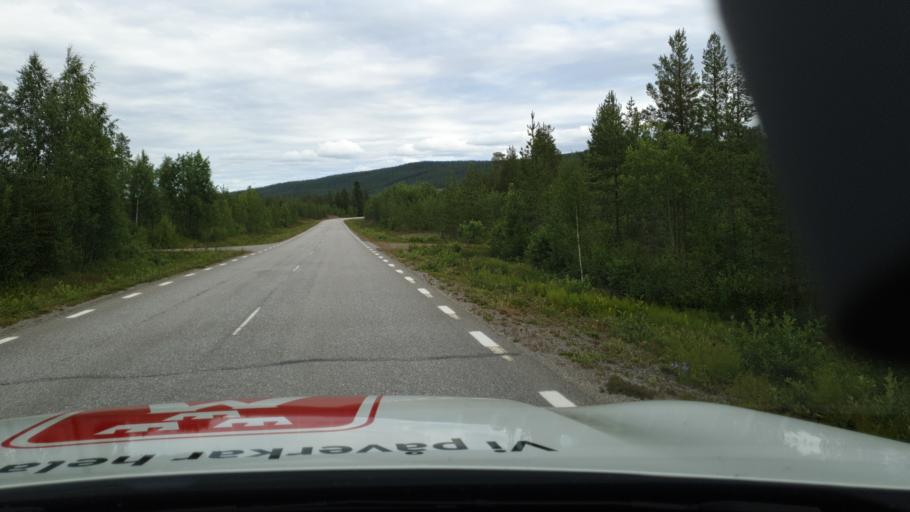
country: SE
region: Vaesterbotten
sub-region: Sorsele Kommun
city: Sorsele
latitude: 65.5368
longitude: 17.3968
